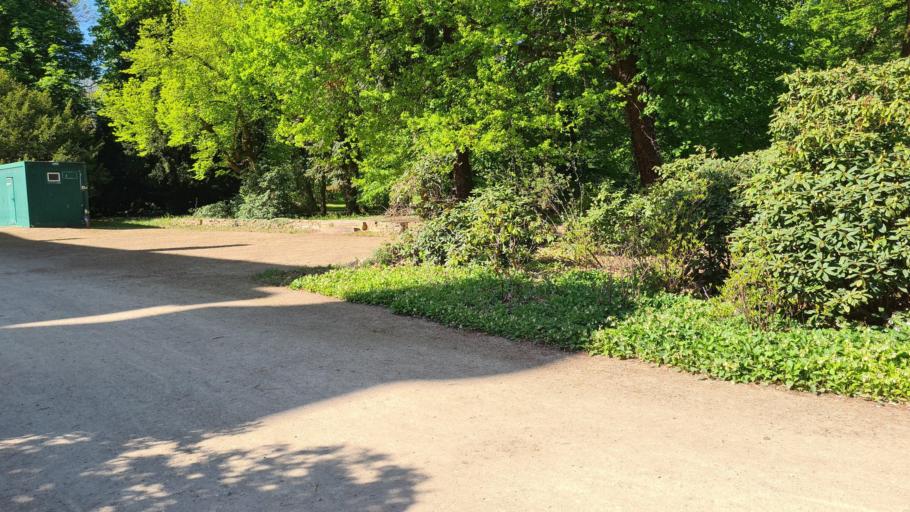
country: DE
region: Brandenburg
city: Altdobern
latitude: 51.6540
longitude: 14.0350
